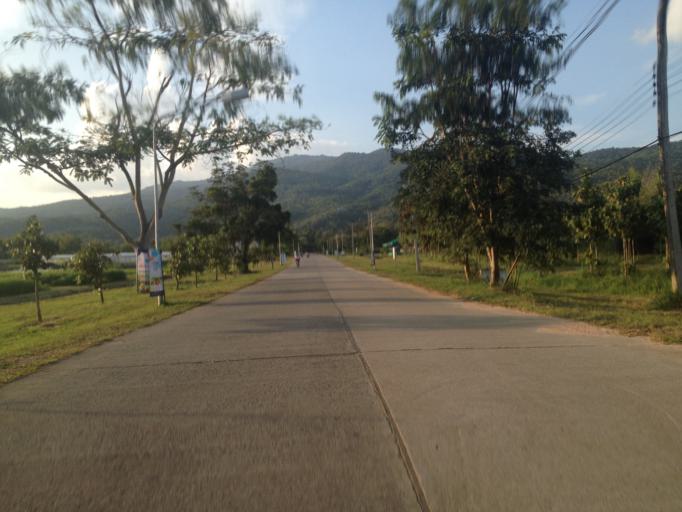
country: TH
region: Chiang Mai
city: Chiang Mai
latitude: 18.7620
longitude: 98.9323
